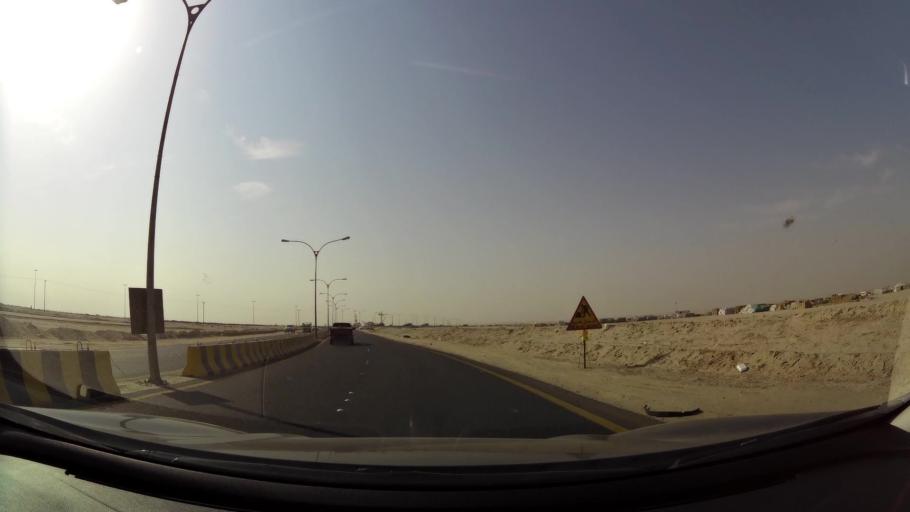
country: KW
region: Al Ahmadi
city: Al Ahmadi
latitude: 28.8936
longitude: 48.0850
